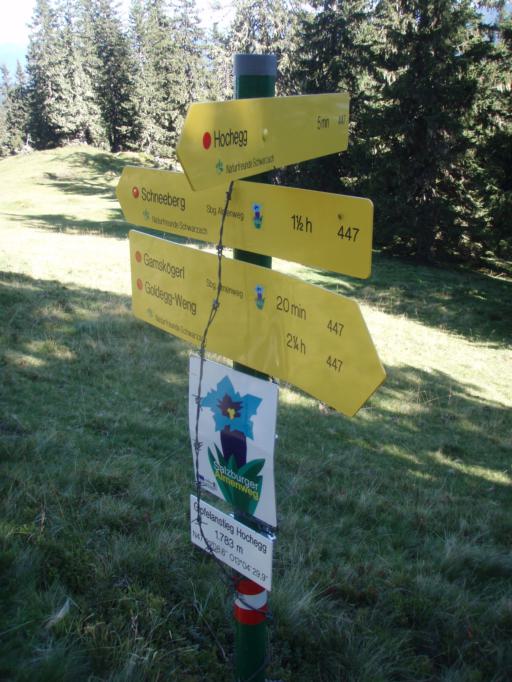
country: AT
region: Salzburg
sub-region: Politischer Bezirk Sankt Johann im Pongau
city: Goldegg
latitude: 47.3519
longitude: 13.0734
